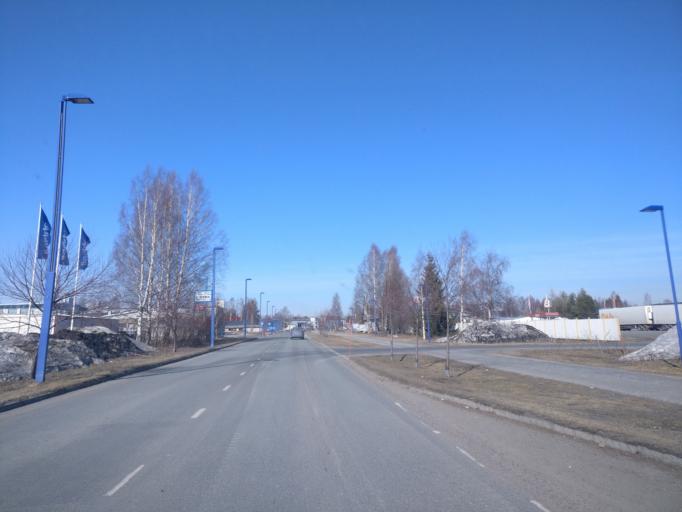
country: FI
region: Lapland
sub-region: Kemi-Tornio
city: Kemi
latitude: 65.7376
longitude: 24.5800
